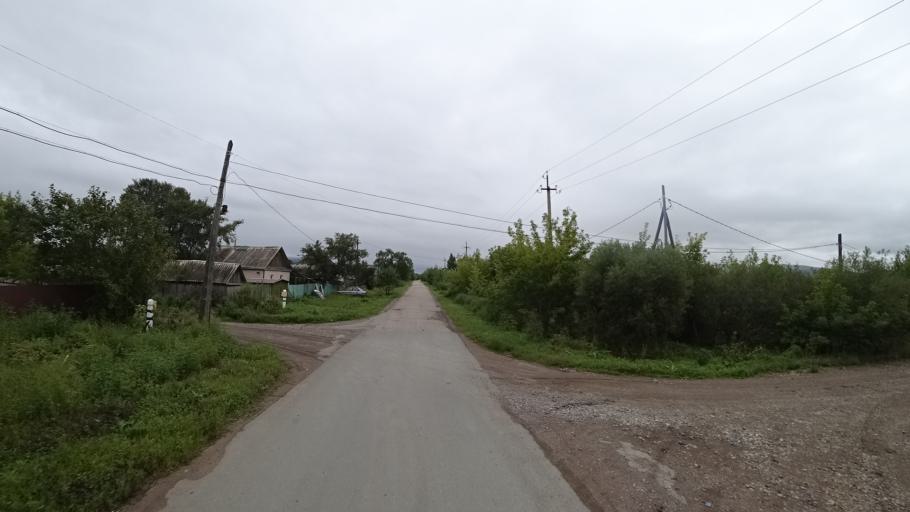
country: RU
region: Primorskiy
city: Chernigovka
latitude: 44.3335
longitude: 132.5903
